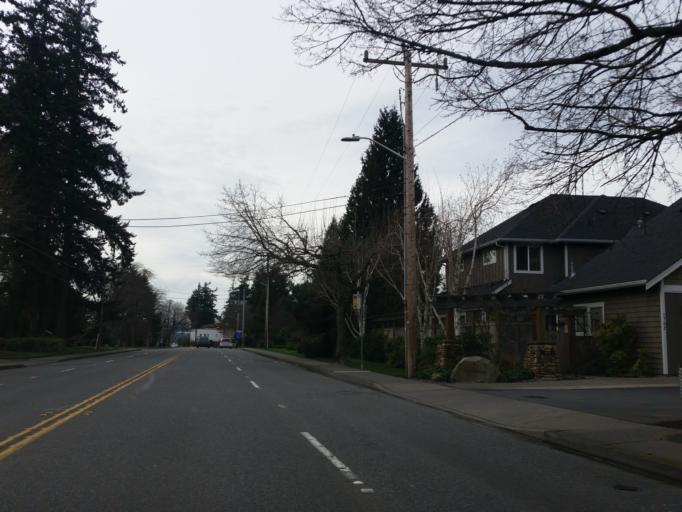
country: US
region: Washington
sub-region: Snohomish County
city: Woodway
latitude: 47.7707
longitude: -122.3794
